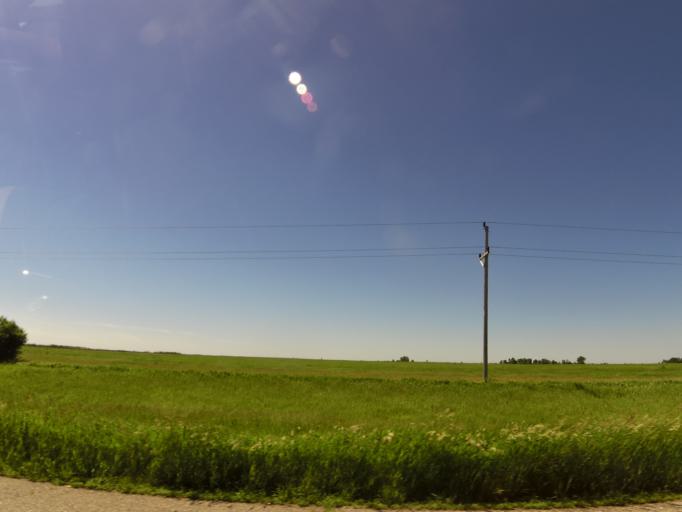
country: US
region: Minnesota
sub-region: Red Lake County
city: Red Lake Falls
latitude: 47.7602
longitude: -96.3308
